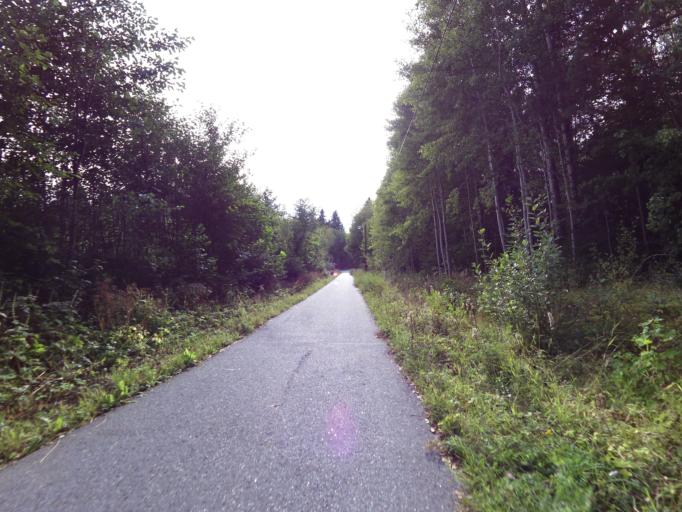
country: SE
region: Gaevleborg
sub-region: Gavle Kommun
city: Gavle
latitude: 60.6758
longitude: 17.2292
